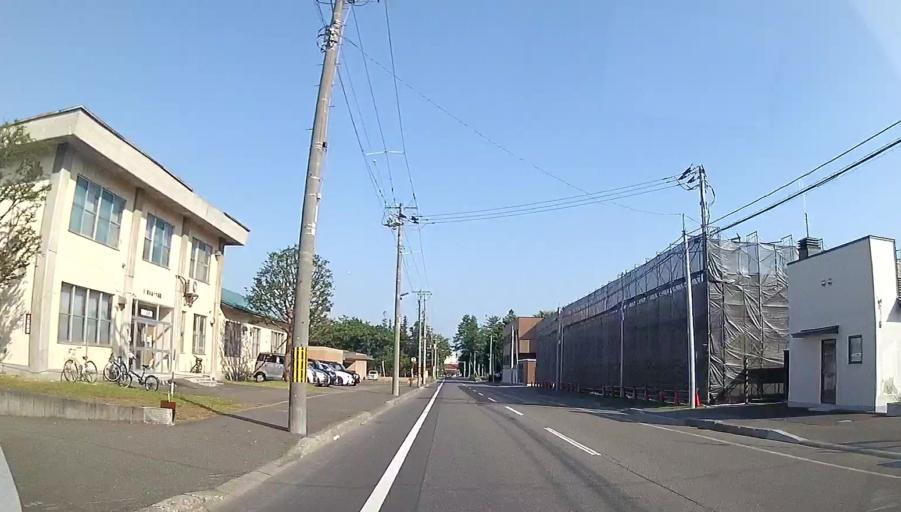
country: JP
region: Hokkaido
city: Otofuke
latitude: 43.0121
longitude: 142.8824
